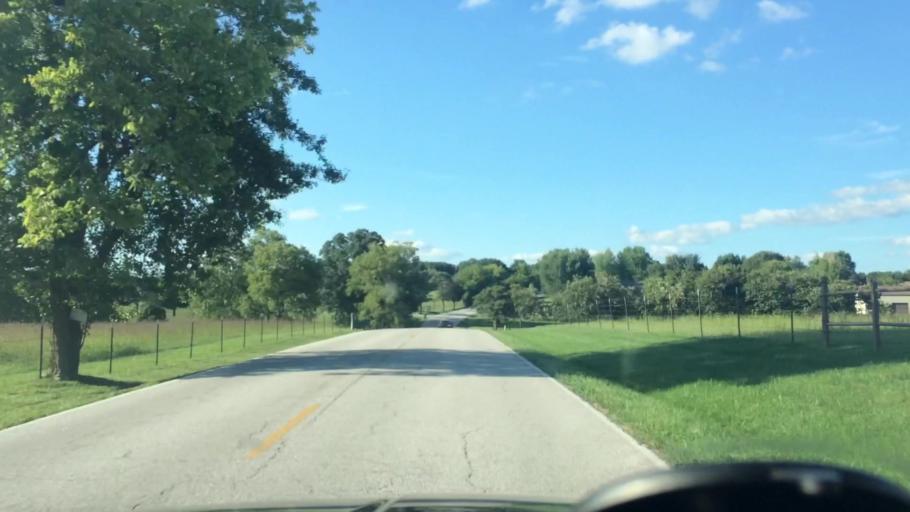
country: US
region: Missouri
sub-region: Greene County
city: Strafford
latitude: 37.2763
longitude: -93.0807
